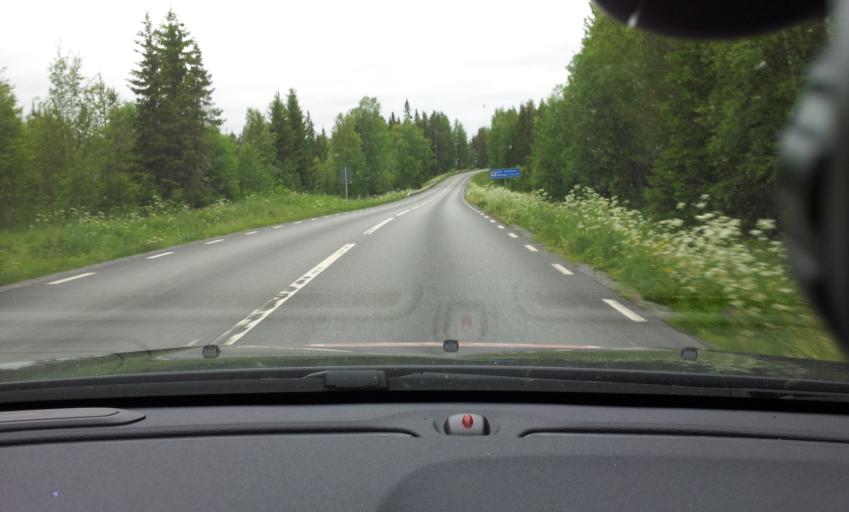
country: SE
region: Jaemtland
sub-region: Bergs Kommun
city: Hoverberg
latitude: 63.0487
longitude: 14.3297
